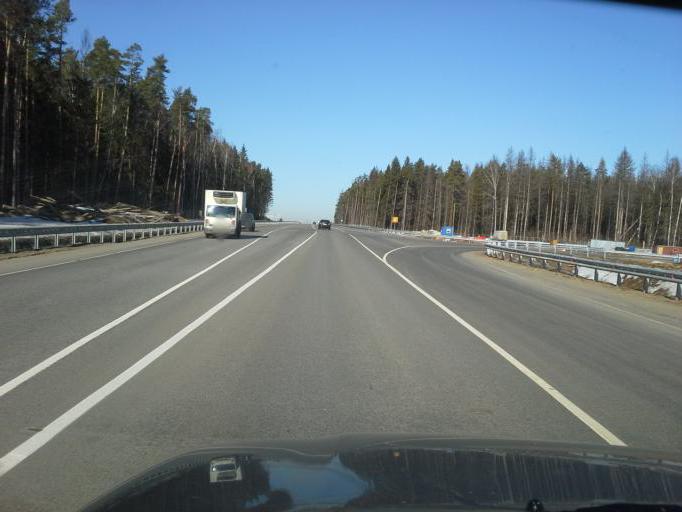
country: RU
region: Moskovskaya
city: Lesnoy Gorodok
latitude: 55.6729
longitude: 37.1708
